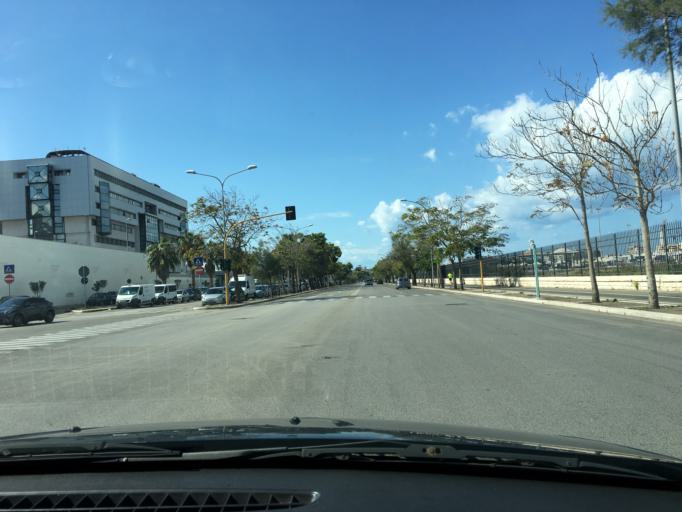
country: IT
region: Apulia
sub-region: Provincia di Bari
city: Bari
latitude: 41.1292
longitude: 16.8518
